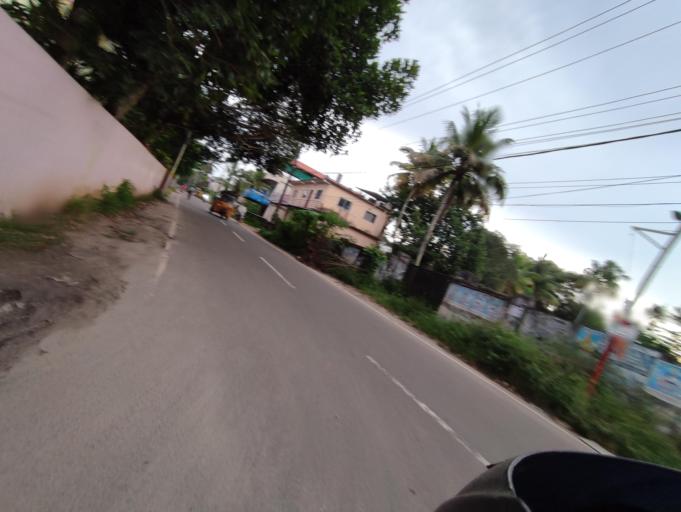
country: IN
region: Kerala
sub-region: Alappuzha
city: Vayalar
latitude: 9.6889
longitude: 76.3340
